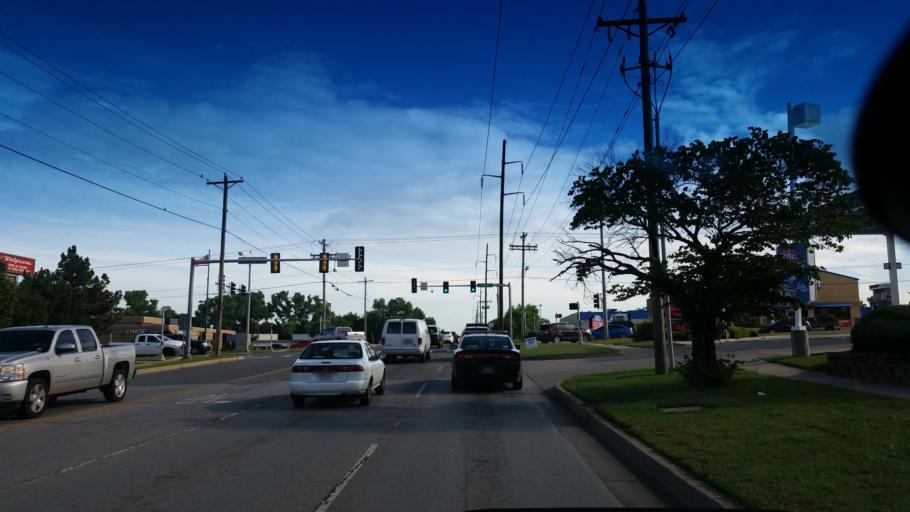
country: US
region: Oklahoma
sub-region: Oklahoma County
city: Edmond
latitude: 35.6404
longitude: -97.5138
